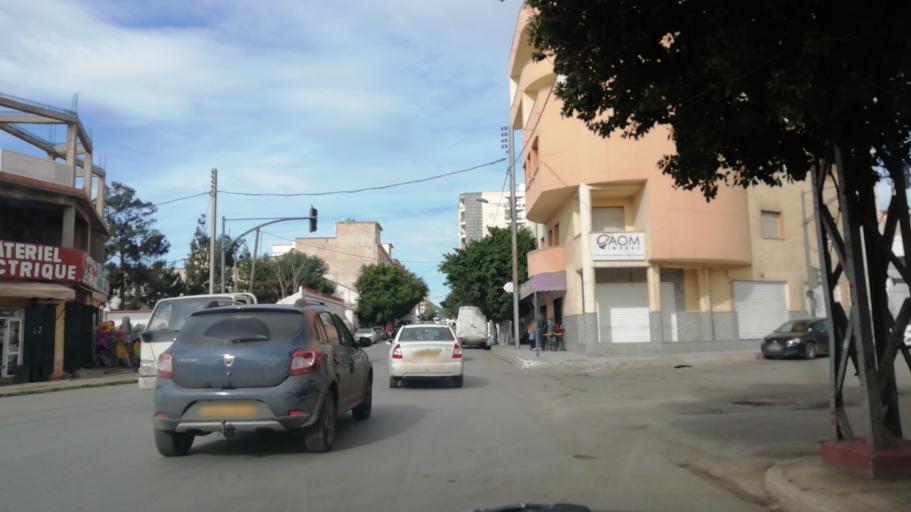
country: DZ
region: Oran
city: Oran
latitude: 35.6896
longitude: -0.6246
